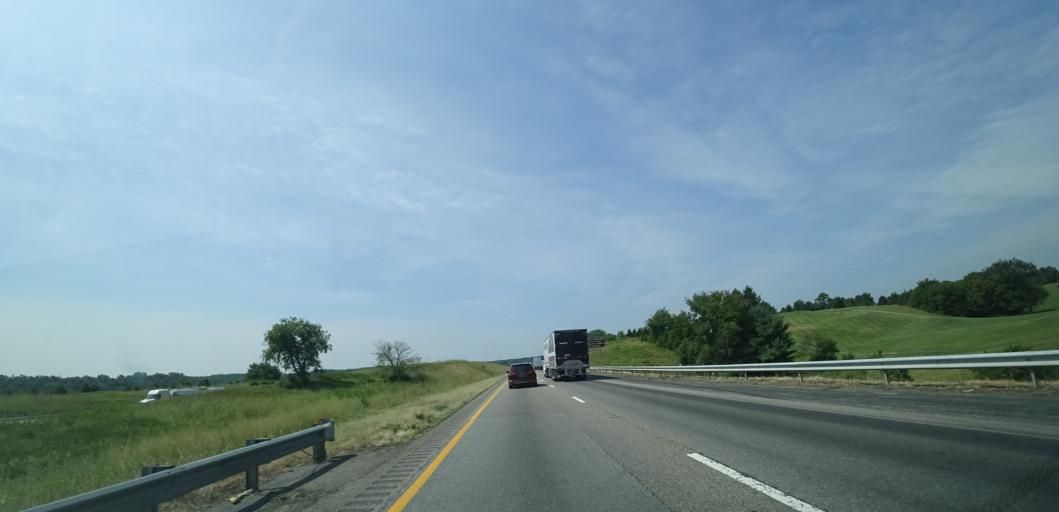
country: US
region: Virginia
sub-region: Augusta County
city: Verona
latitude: 38.1735
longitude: -79.0036
